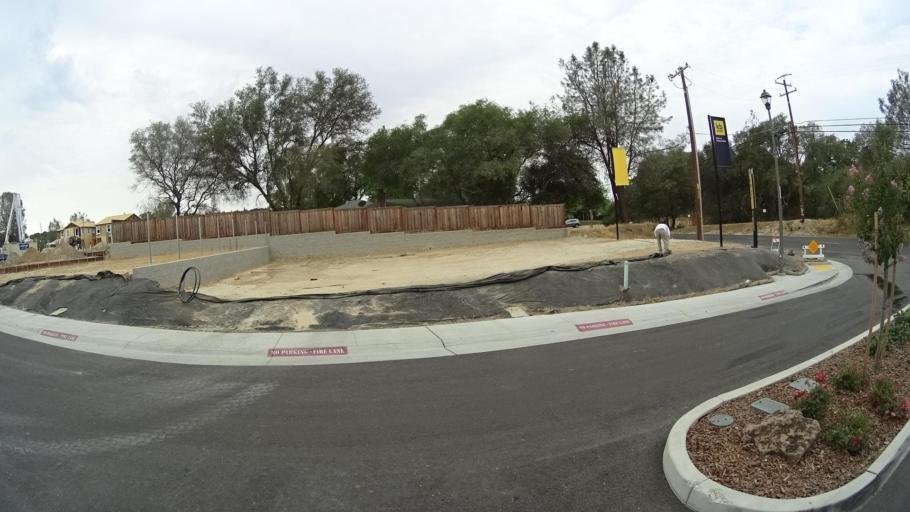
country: US
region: California
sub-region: Placer County
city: Rocklin
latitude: 38.7865
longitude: -121.2193
